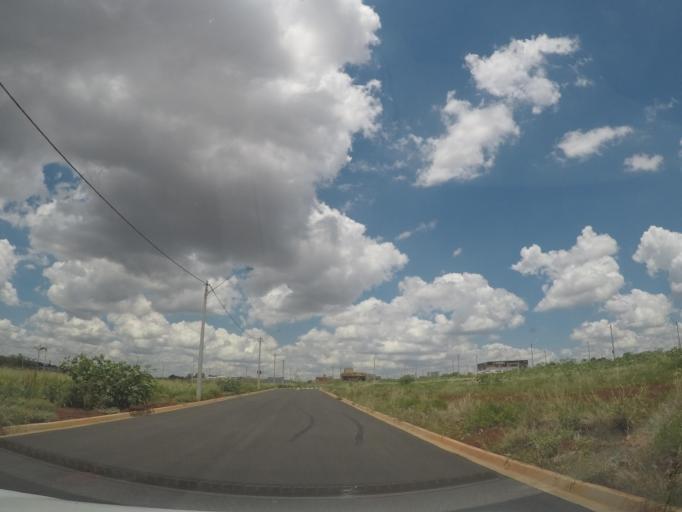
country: BR
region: Sao Paulo
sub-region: Hortolandia
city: Hortolandia
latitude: -22.8381
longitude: -47.2332
